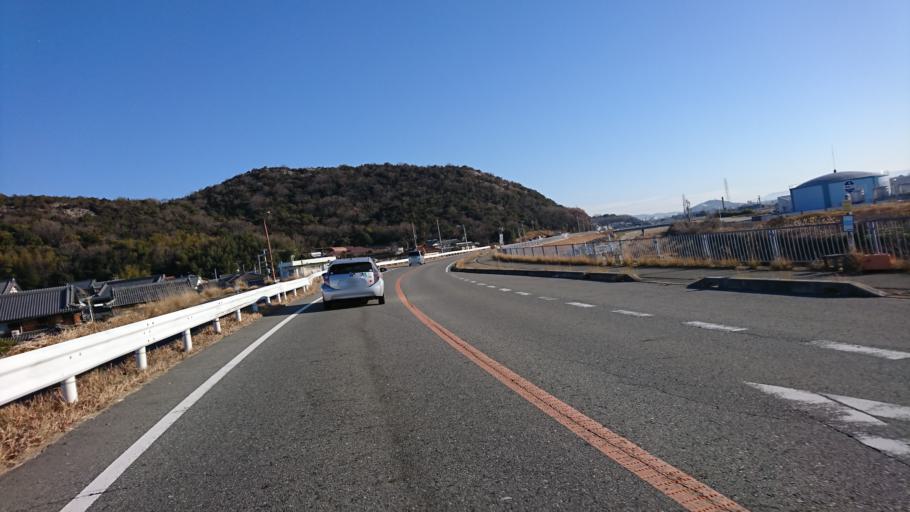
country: JP
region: Hyogo
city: Kakogawacho-honmachi
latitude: 34.7846
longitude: 134.8467
